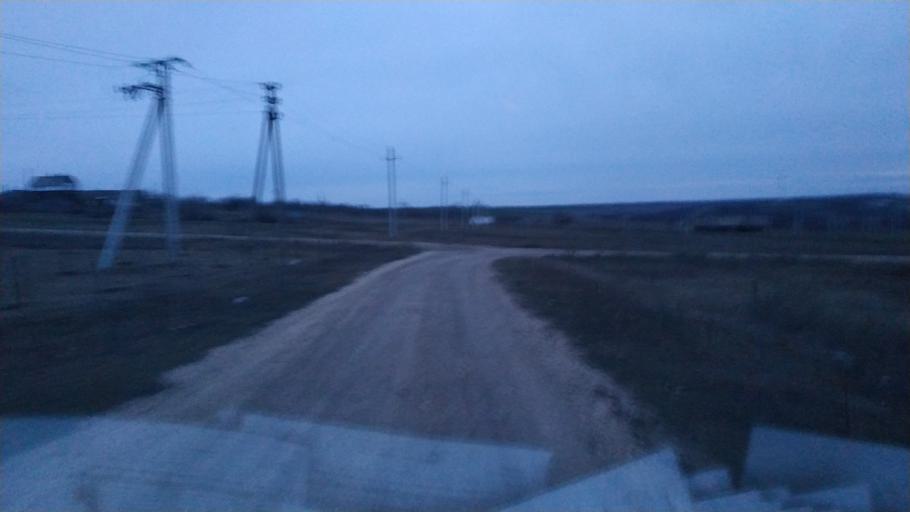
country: MD
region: Causeni
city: Causeni
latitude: 46.4923
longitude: 29.3980
